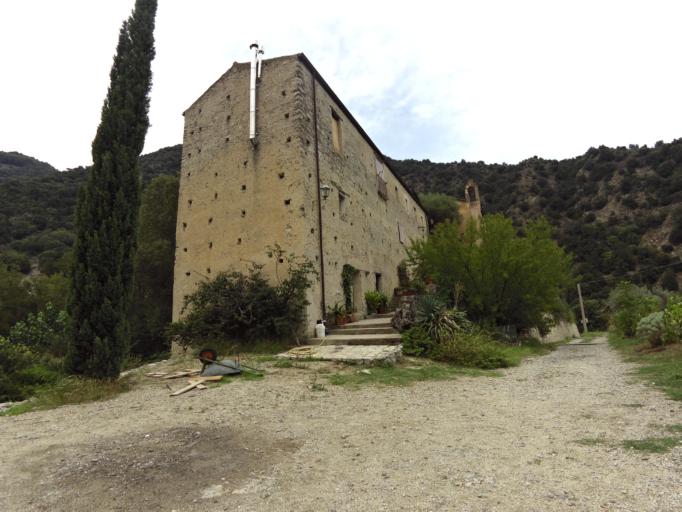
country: IT
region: Calabria
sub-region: Provincia di Reggio Calabria
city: Caulonia
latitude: 38.4243
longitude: 16.3771
